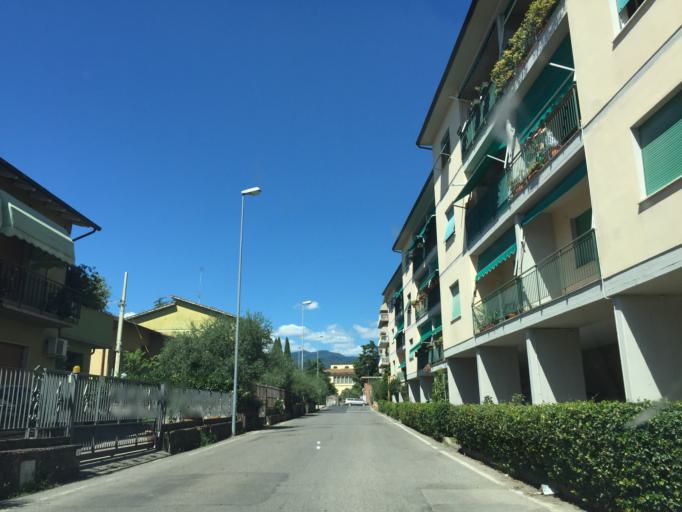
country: IT
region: Tuscany
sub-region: Provincia di Pistoia
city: Pistoia
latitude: 43.9481
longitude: 10.9081
